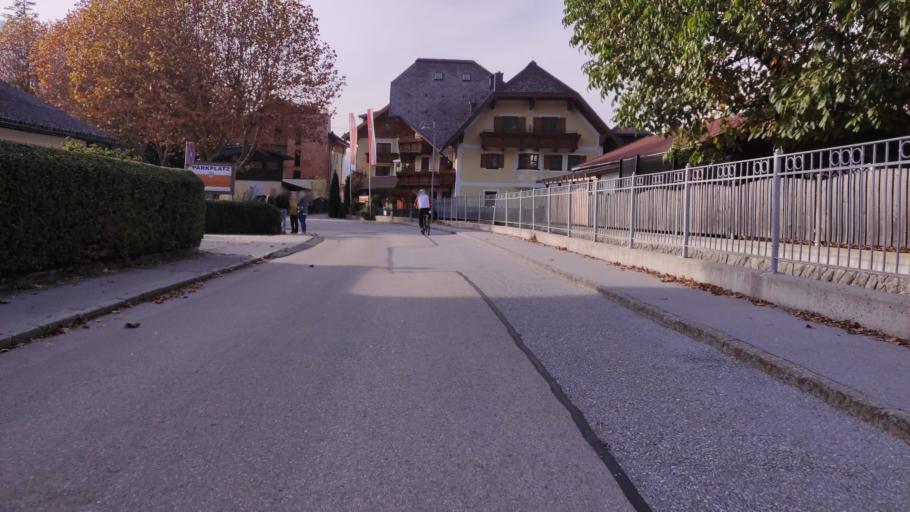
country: AT
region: Salzburg
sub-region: Politischer Bezirk Salzburg-Umgebung
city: Fuschl am See
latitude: 47.7968
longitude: 13.3001
